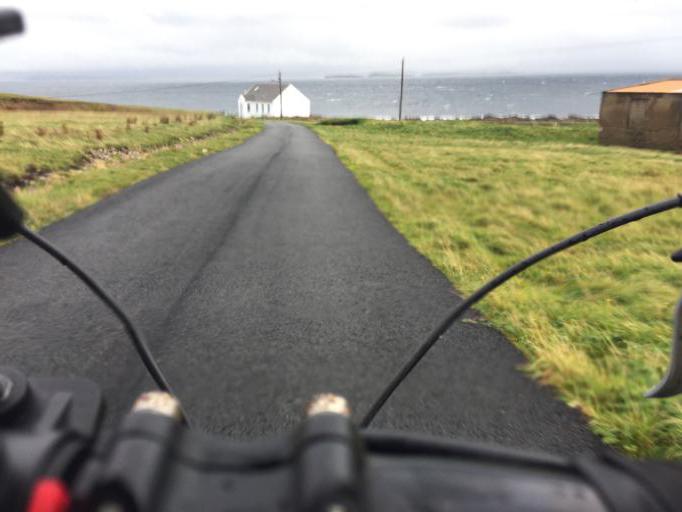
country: IE
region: Ulster
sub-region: County Donegal
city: Derrybeg
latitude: 55.2562
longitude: -8.1965
